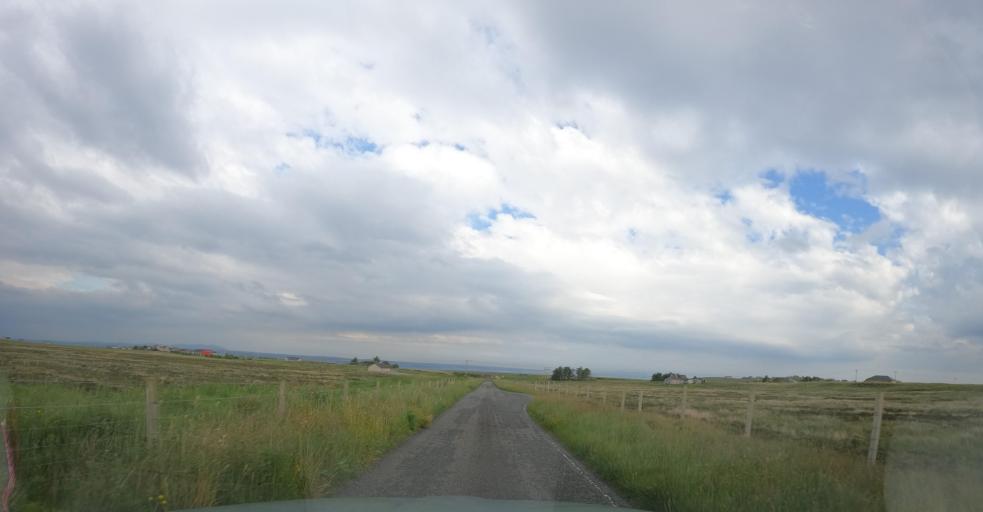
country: GB
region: Scotland
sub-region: Eilean Siar
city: Stornoway
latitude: 58.2071
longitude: -6.2491
